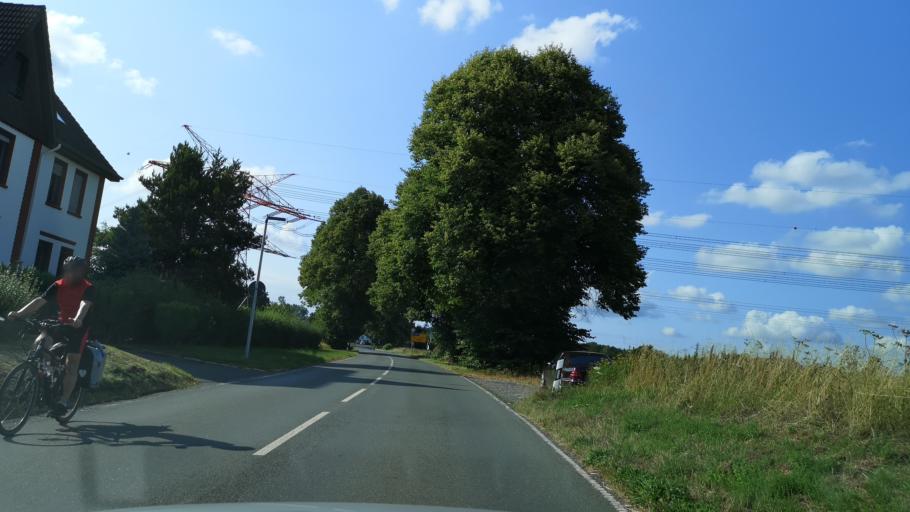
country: DE
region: North Rhine-Westphalia
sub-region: Regierungsbezirk Arnsberg
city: Holzwickede
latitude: 51.4606
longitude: 7.6230
